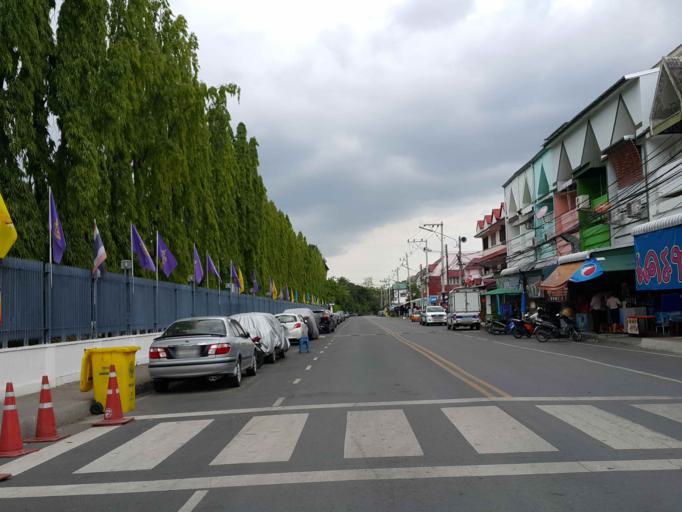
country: TH
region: Chiang Mai
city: Chiang Mai
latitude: 18.7654
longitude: 99.0212
